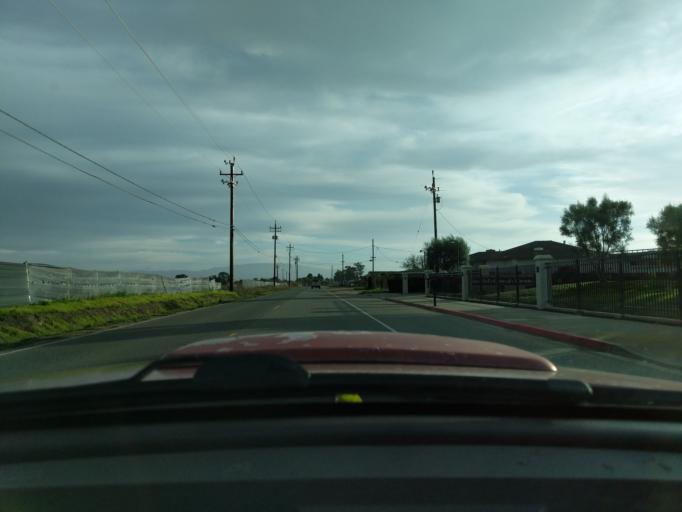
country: US
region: California
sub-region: Monterey County
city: Prunedale
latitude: 36.7397
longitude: -121.6567
